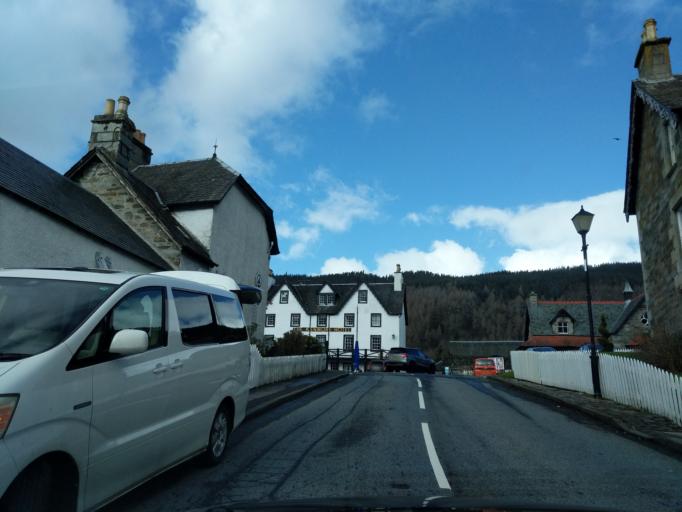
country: GB
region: Scotland
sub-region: Perth and Kinross
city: Aberfeldy
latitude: 56.5849
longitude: -3.9982
